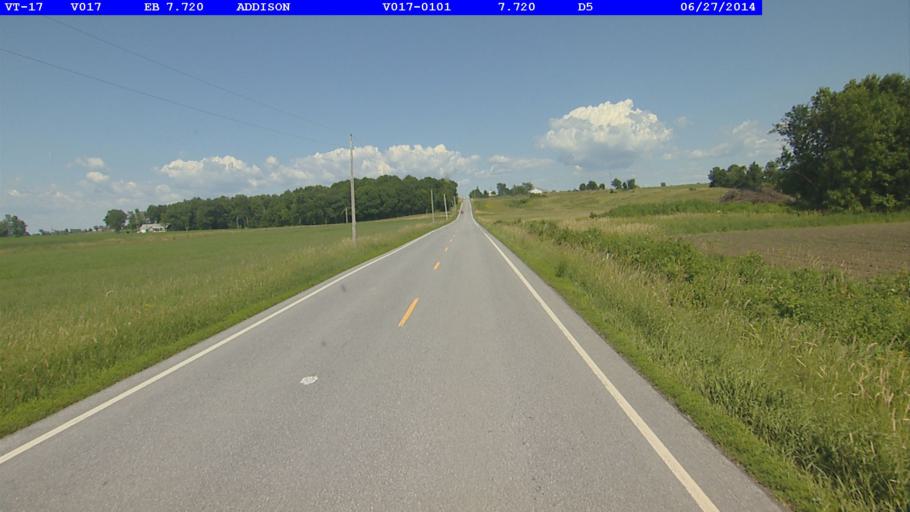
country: US
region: Vermont
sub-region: Addison County
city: Vergennes
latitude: 44.0879
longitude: -73.3155
